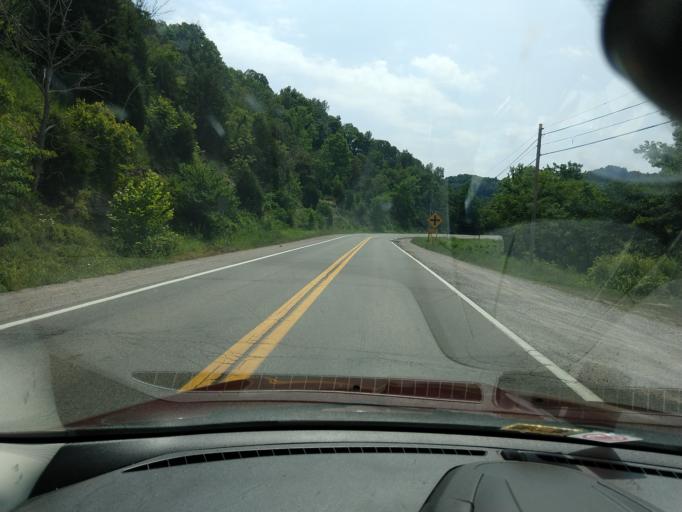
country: US
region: West Virginia
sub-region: Jackson County
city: Ravenswood
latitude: 38.8690
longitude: -81.8200
